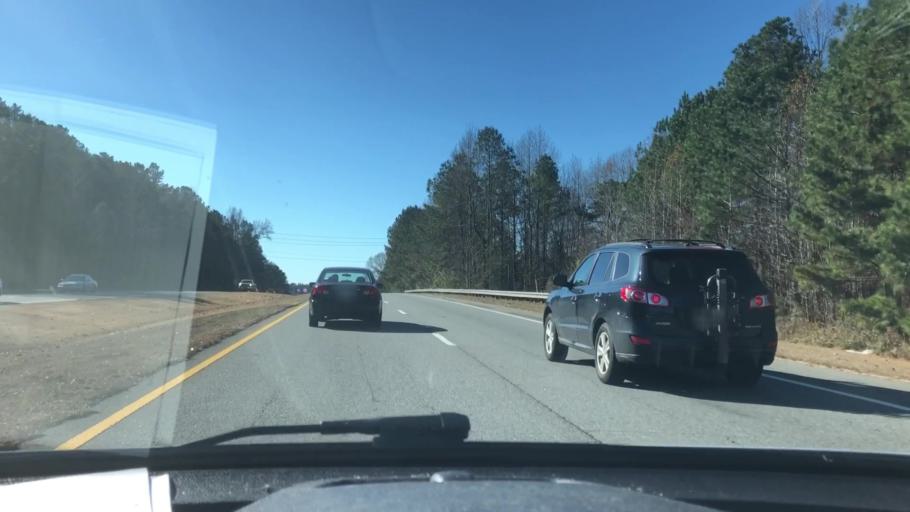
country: US
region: Georgia
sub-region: Gwinnett County
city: Norcross
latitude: 33.9612
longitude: -84.2281
